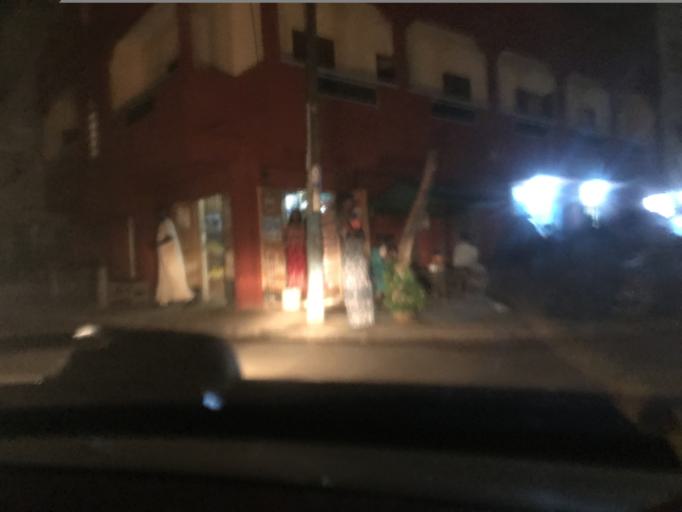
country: SN
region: Dakar
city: Grand Dakar
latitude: 14.7529
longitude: -17.4503
